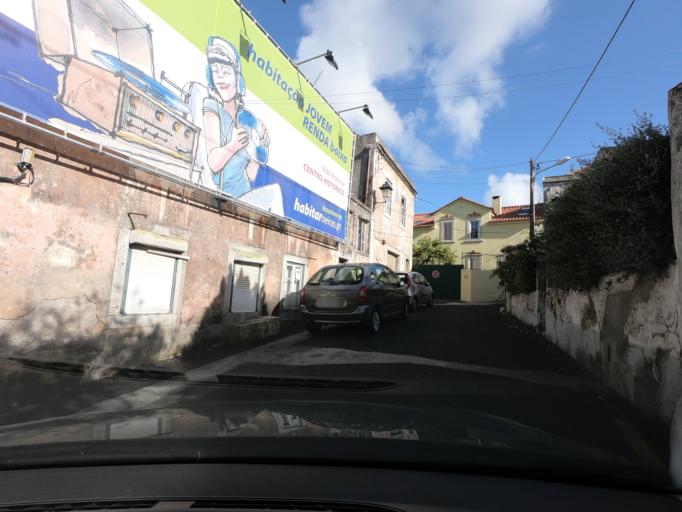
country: PT
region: Lisbon
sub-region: Oeiras
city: Oeiras
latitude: 38.6934
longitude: -9.3127
